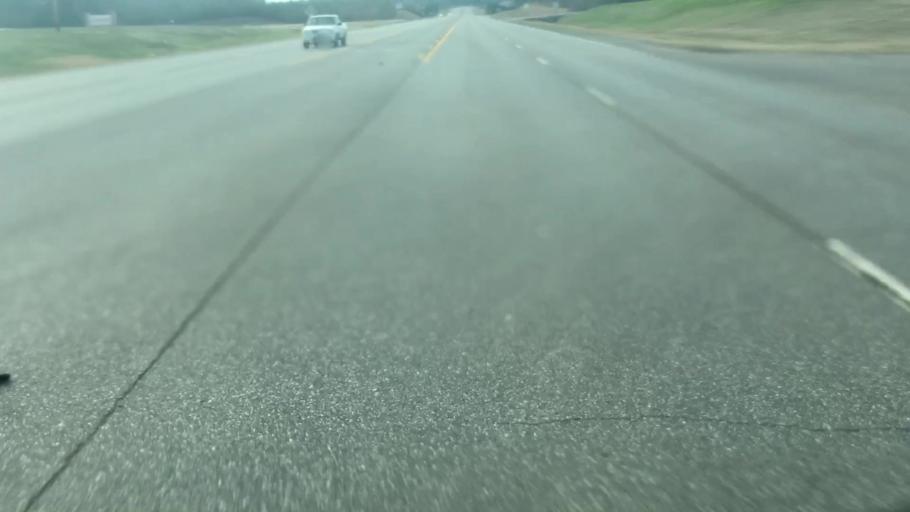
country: US
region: Alabama
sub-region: Walker County
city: Jasper
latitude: 33.8121
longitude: -87.2336
